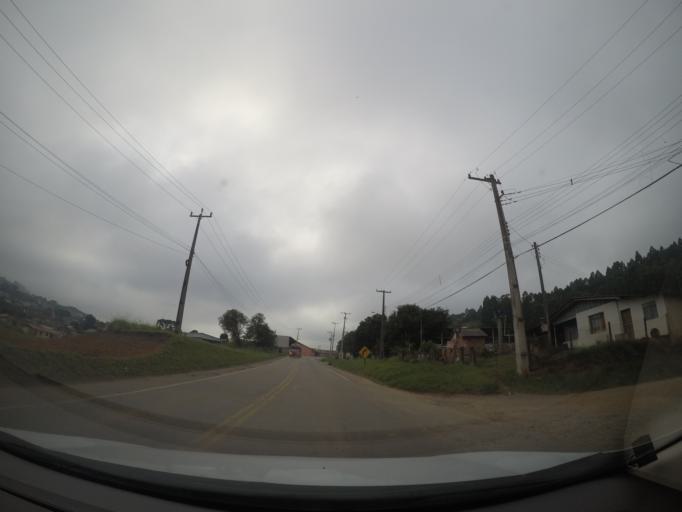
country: BR
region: Parana
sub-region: Colombo
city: Colombo
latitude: -25.2943
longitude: -49.2444
